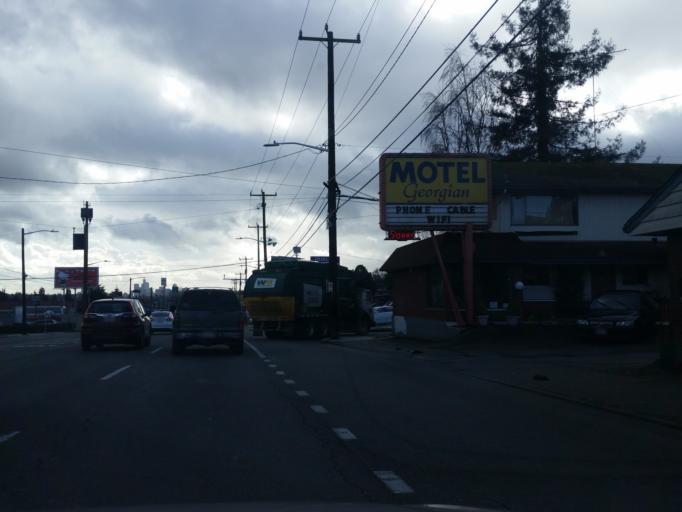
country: US
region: Washington
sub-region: King County
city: Shoreline
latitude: 47.6931
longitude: -122.3446
